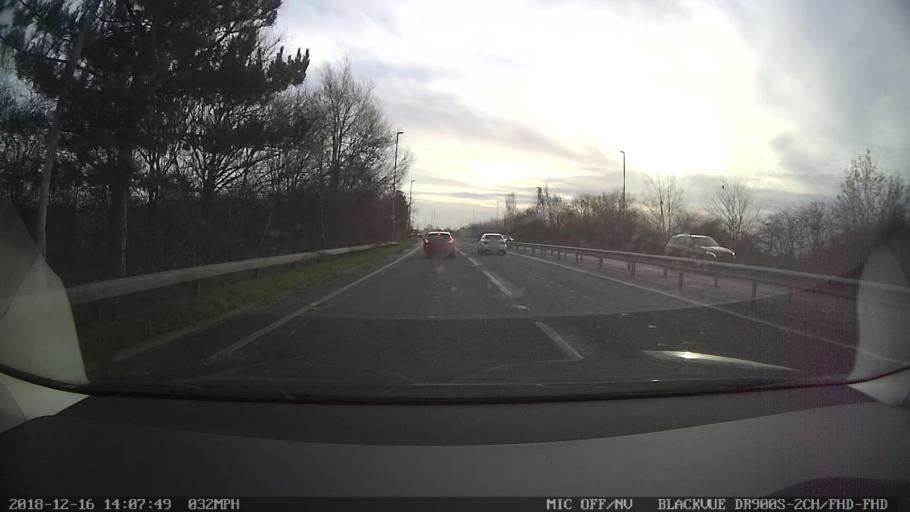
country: GB
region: England
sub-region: Borough of Stockport
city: Cheadle Hulme
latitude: 53.3681
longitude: -2.2100
